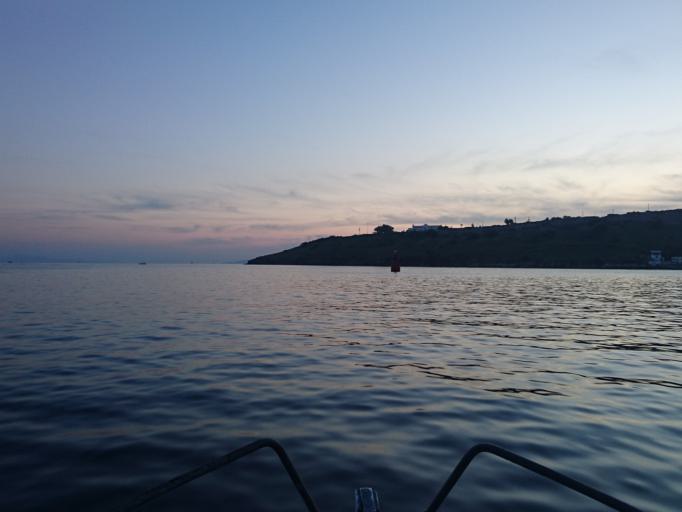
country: TR
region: Mugla
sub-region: Bodrum
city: Bodrum
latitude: 37.0300
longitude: 27.4231
